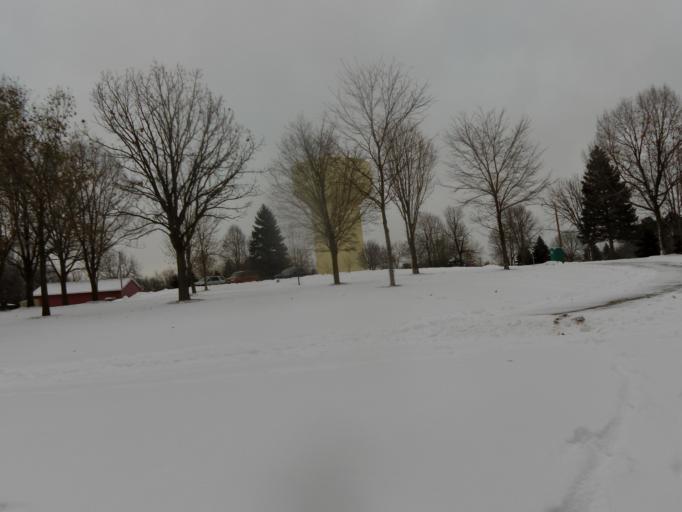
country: US
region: Minnesota
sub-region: Dakota County
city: Inver Grove Heights
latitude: 44.8656
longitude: -93.0741
